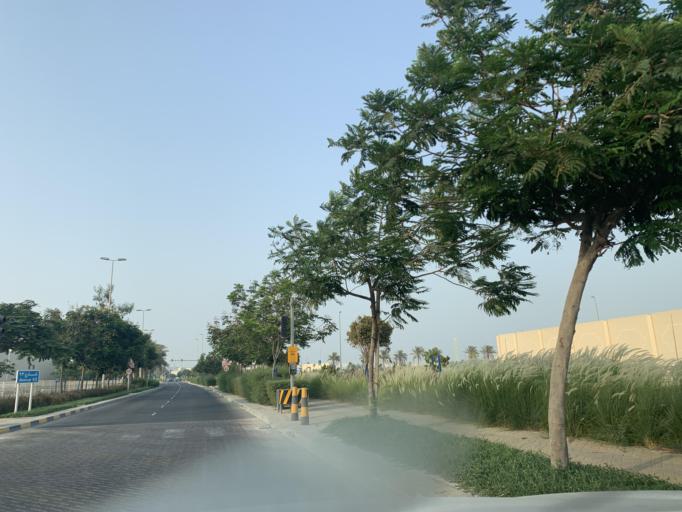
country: BH
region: Manama
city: Jidd Hafs
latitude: 26.2259
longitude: 50.4439
